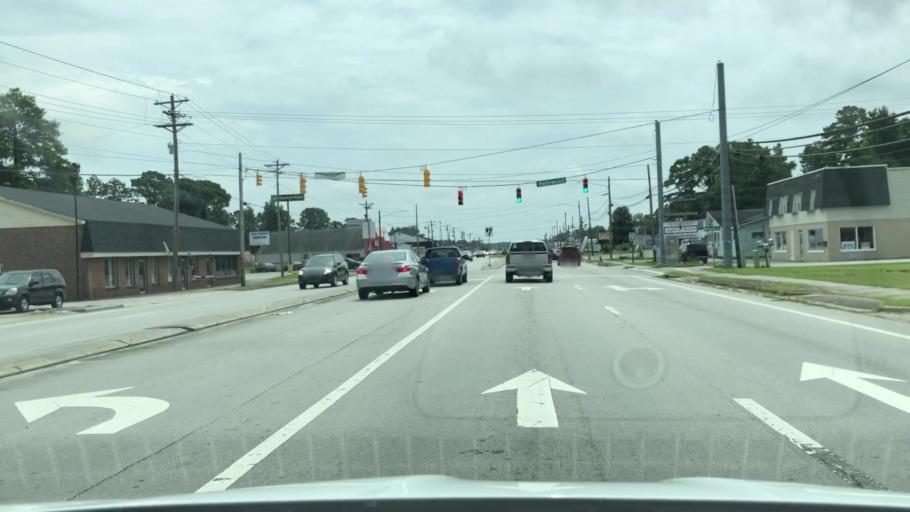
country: US
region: North Carolina
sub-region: Craven County
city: Havelock
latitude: 34.8712
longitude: -76.9016
